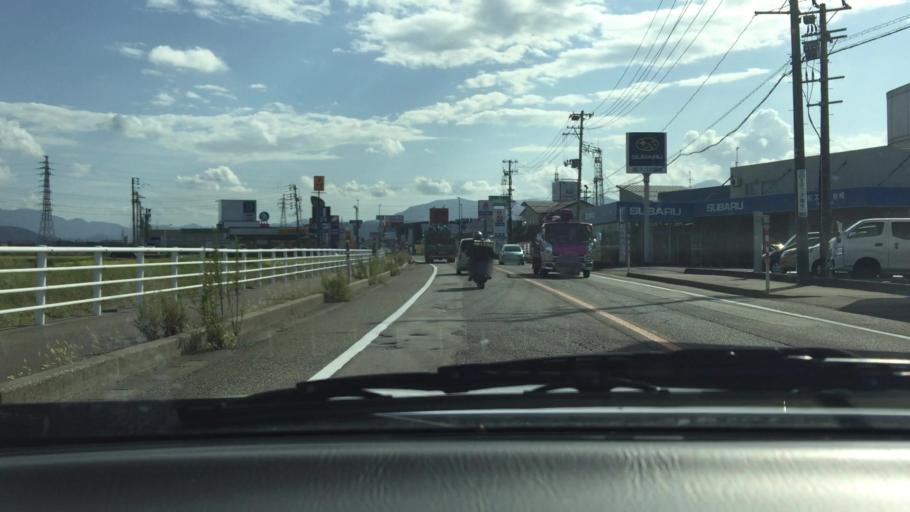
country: JP
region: Niigata
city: Kashiwazaki
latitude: 37.3815
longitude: 138.5818
